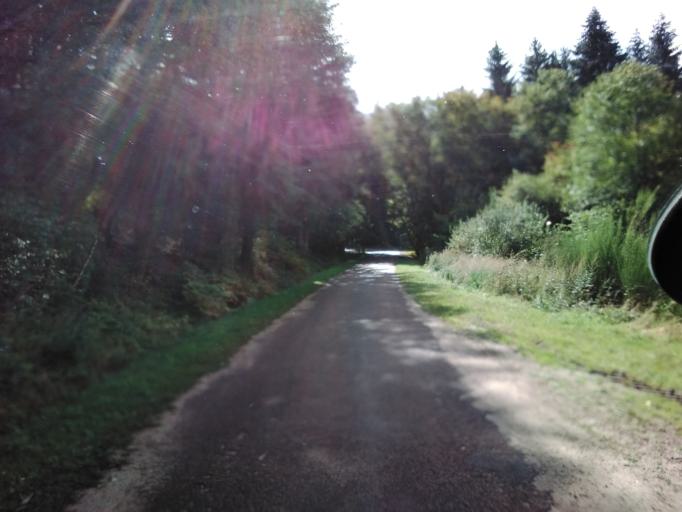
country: FR
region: Bourgogne
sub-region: Departement de la Nievre
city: Lormes
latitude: 47.3217
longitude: 3.8967
